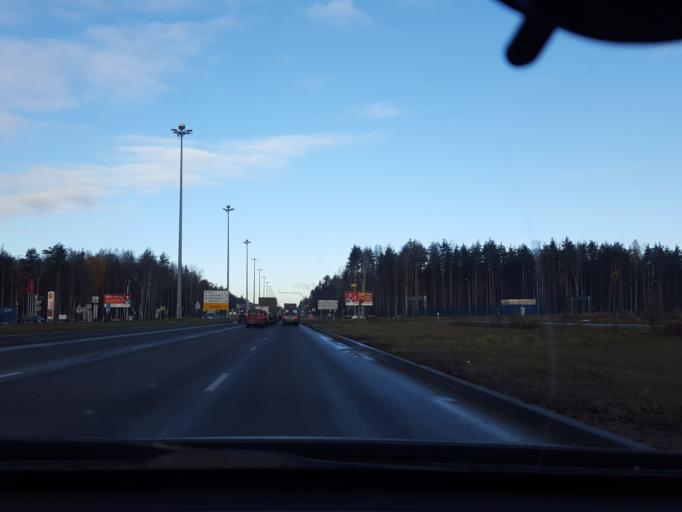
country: RU
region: Leningrad
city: Untolovo
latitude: 60.0513
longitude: 30.2290
